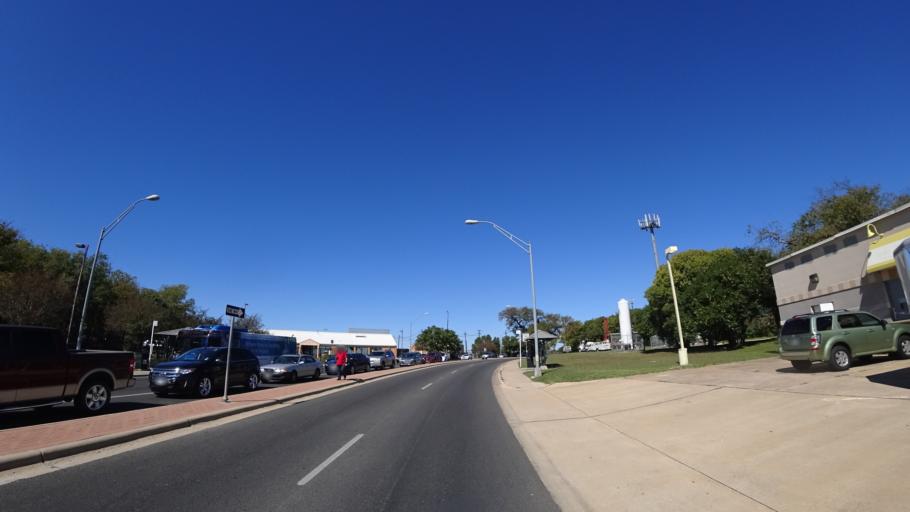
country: US
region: Texas
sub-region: Travis County
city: Austin
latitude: 30.3264
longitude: -97.7267
